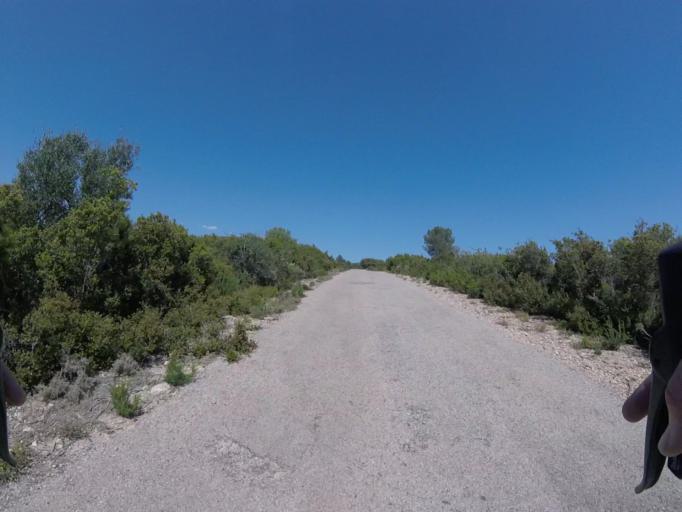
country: ES
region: Valencia
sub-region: Provincia de Castello
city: Sierra-Engarceran
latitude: 40.2319
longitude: -0.0250
